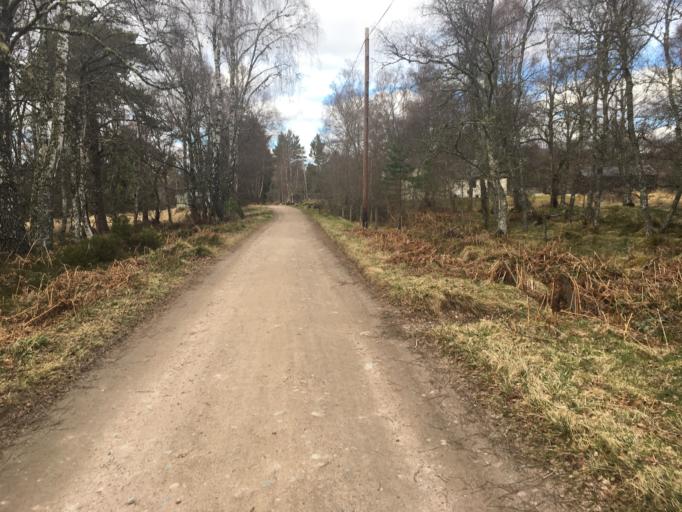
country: GB
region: Scotland
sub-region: Highland
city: Aviemore
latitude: 57.1662
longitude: -3.8114
